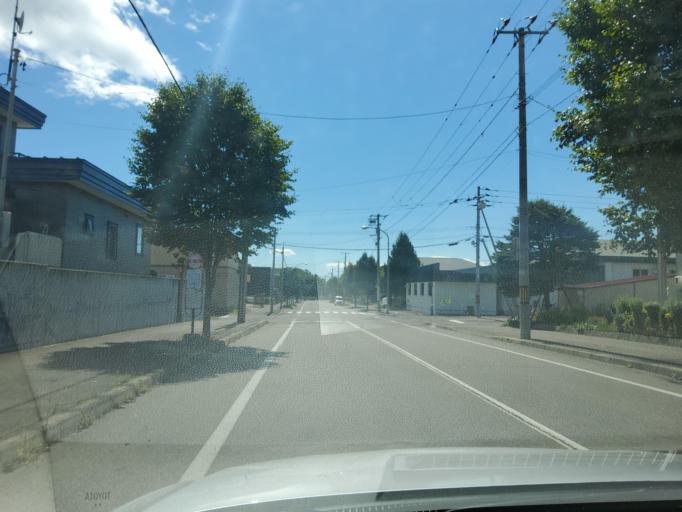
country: JP
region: Hokkaido
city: Obihiro
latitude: 42.9494
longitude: 143.1960
